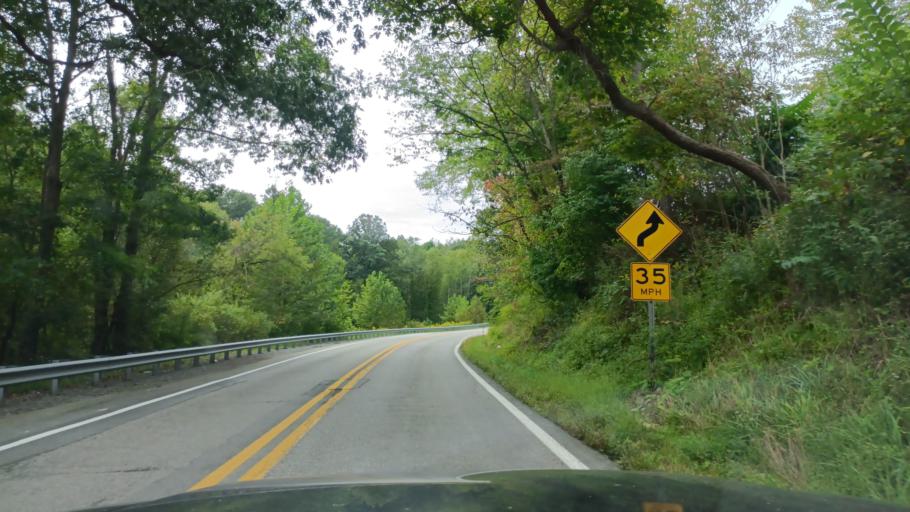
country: US
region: West Virginia
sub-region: Taylor County
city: Grafton
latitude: 39.3184
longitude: -80.1251
